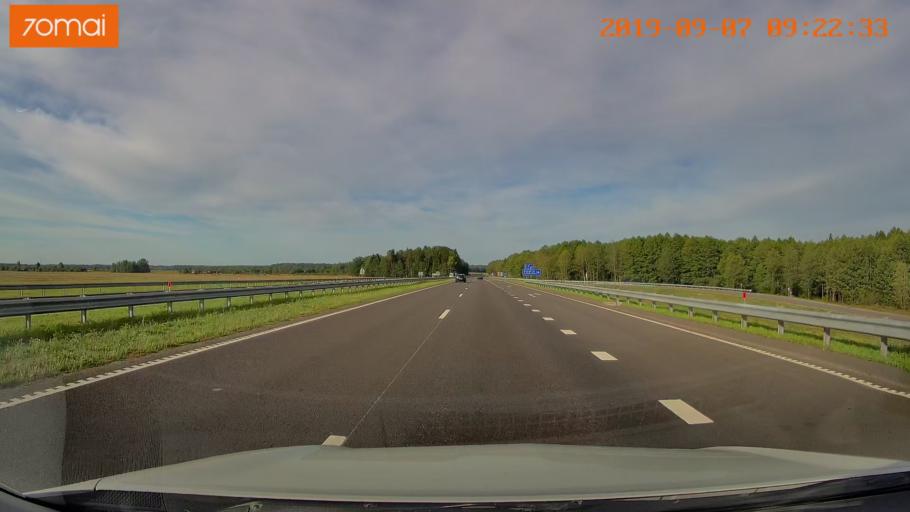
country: BY
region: Grodnenskaya
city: Lyubcha
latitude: 53.9550
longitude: 26.1814
